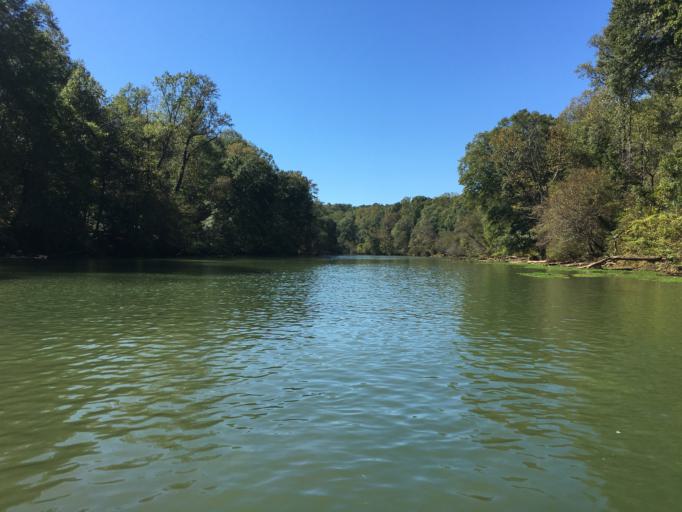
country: US
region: Georgia
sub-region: Fulton County
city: Johns Creek
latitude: 33.9993
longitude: -84.2444
